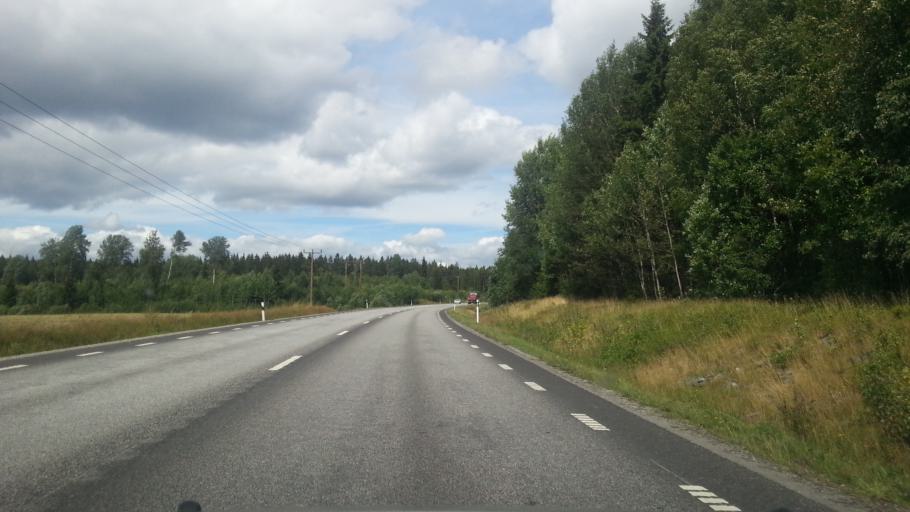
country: SE
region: OErebro
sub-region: Lindesbergs Kommun
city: Lindesberg
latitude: 59.5901
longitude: 15.1872
